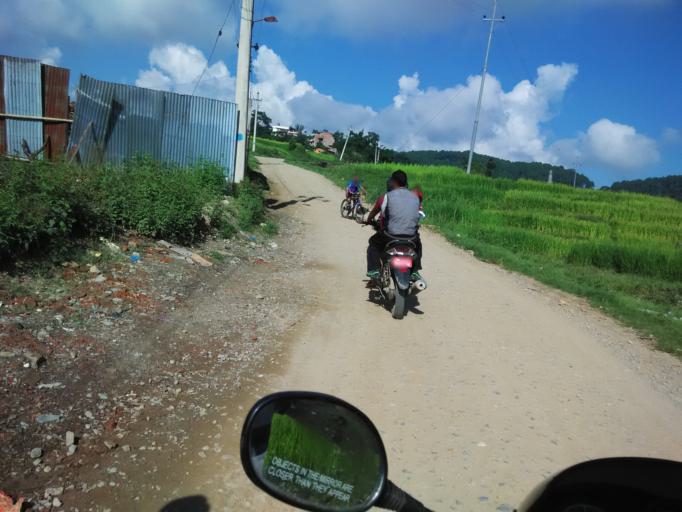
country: NP
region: Central Region
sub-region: Bagmati Zone
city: Patan
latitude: 27.6066
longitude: 85.3481
